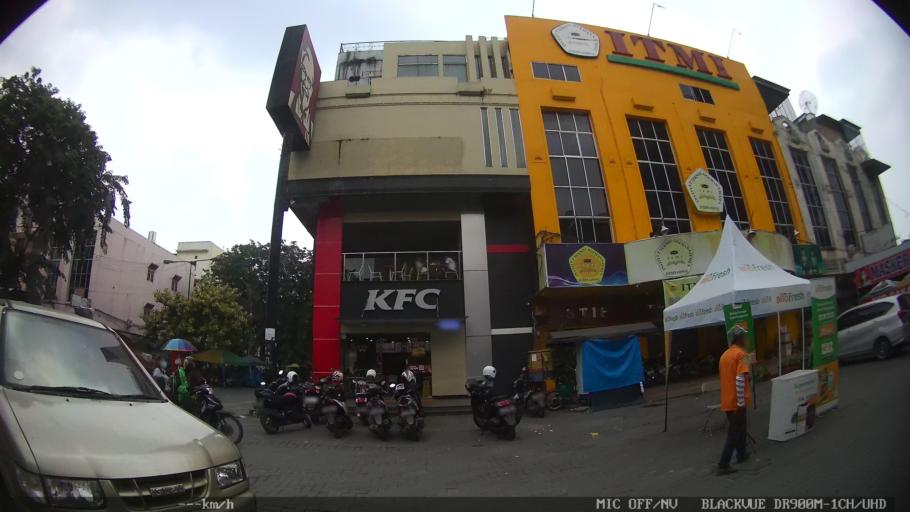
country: ID
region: North Sumatra
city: Medan
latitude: 3.5861
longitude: 98.7031
